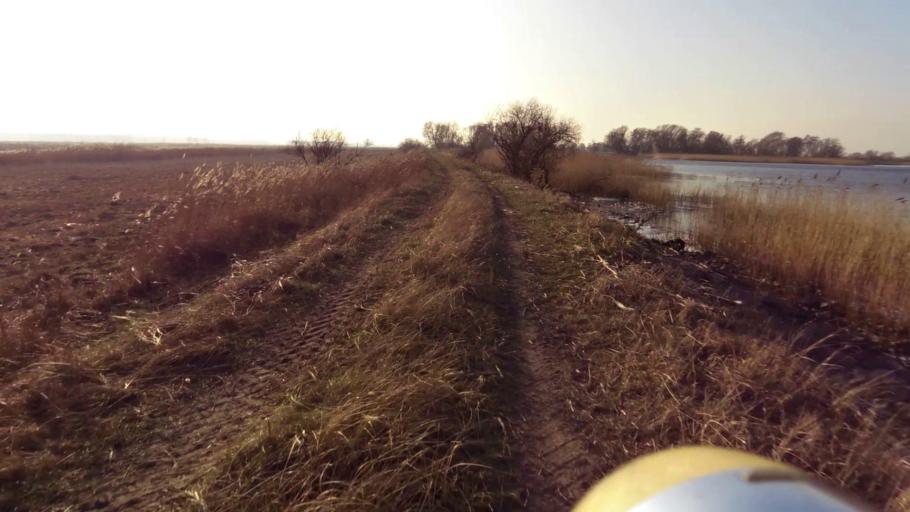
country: PL
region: West Pomeranian Voivodeship
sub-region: Powiat kamienski
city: Wolin
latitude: 53.7557
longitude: 14.5847
